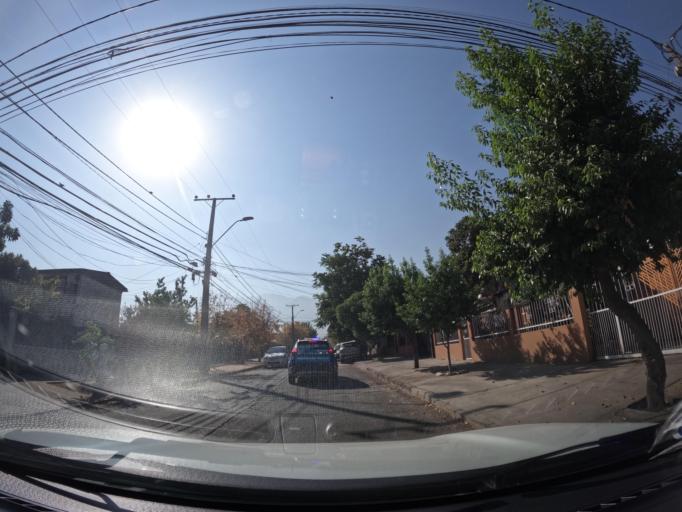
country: CL
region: Santiago Metropolitan
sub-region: Provincia de Santiago
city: Villa Presidente Frei, Nunoa, Santiago, Chile
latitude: -33.5095
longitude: -70.5713
